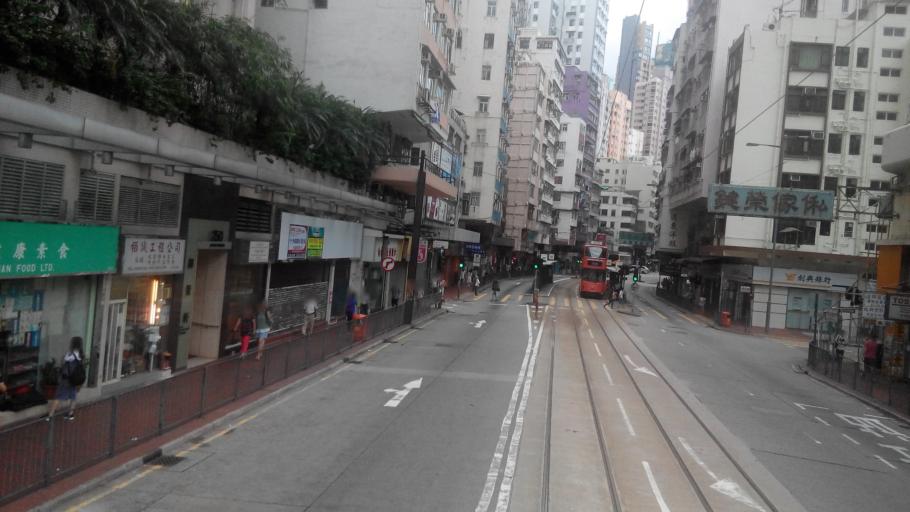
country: HK
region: Wanchai
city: Wan Chai
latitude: 22.2803
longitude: 114.2250
